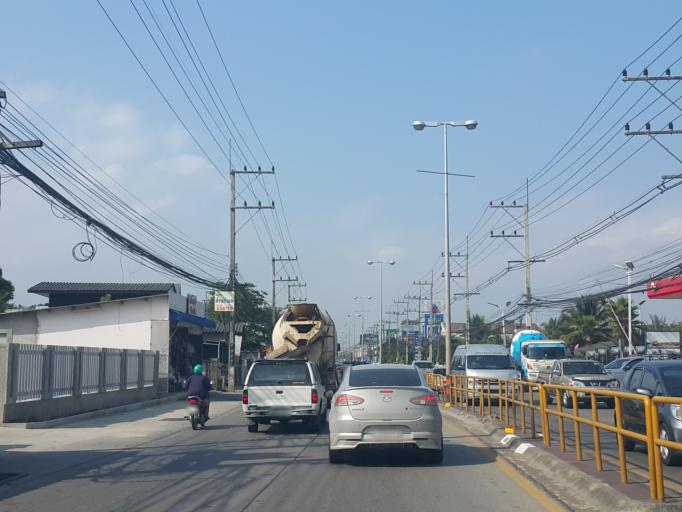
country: TH
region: Chiang Mai
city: San Sai
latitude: 18.9173
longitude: 98.9439
